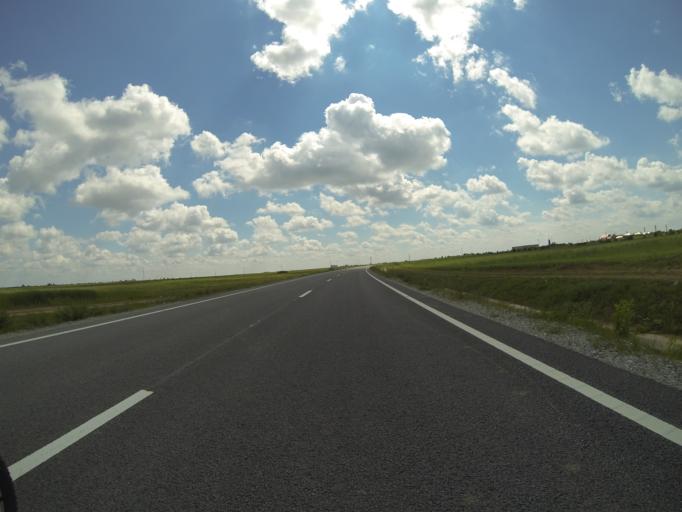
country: RO
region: Dolj
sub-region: Comuna Carcea
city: Carcea
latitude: 44.2664
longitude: 23.9112
